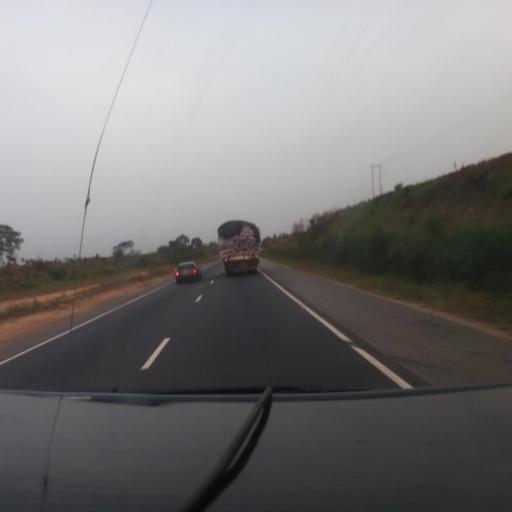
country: GH
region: Eastern
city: Nsawam
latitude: 5.8881
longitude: -0.3797
